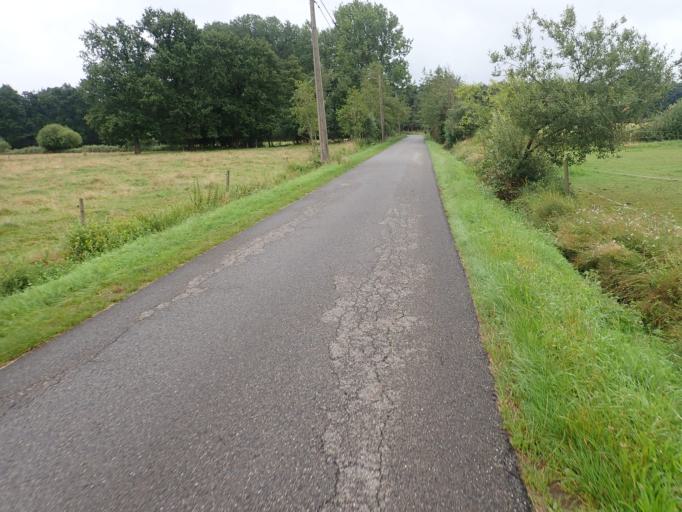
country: BE
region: Flanders
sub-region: Provincie Antwerpen
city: Zoersel
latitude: 51.2519
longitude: 4.7315
